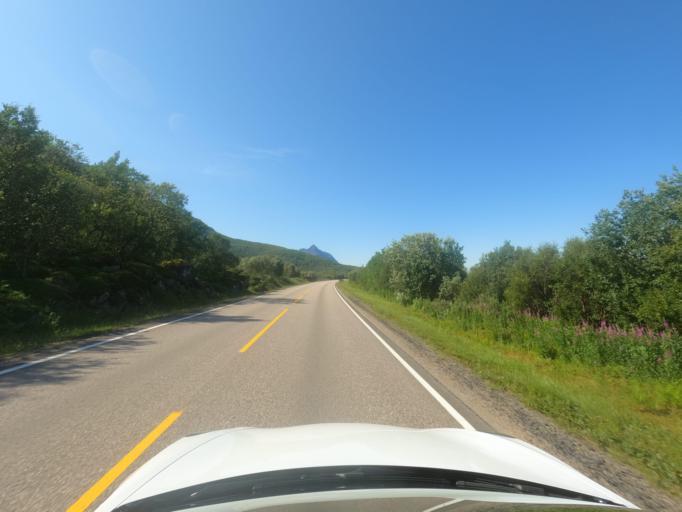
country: NO
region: Nordland
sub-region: Hadsel
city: Stokmarknes
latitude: 68.4458
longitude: 14.9404
